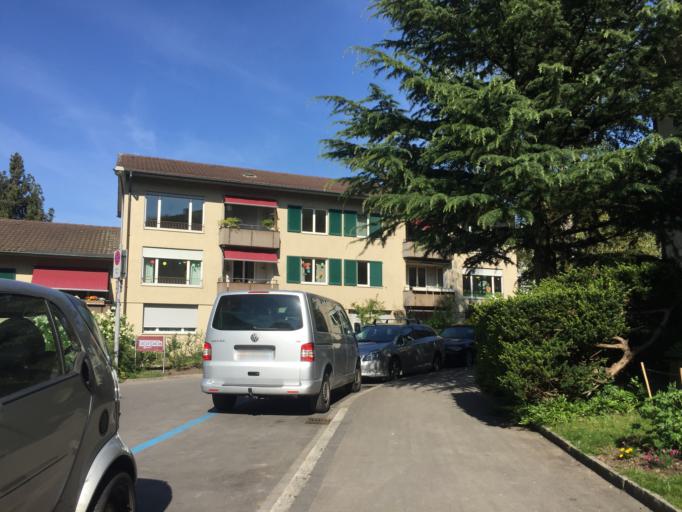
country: CH
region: Zurich
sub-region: Bezirk Zuerich
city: Zuerich (Kreis 11) / Oerlikon
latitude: 47.4010
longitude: 8.5463
